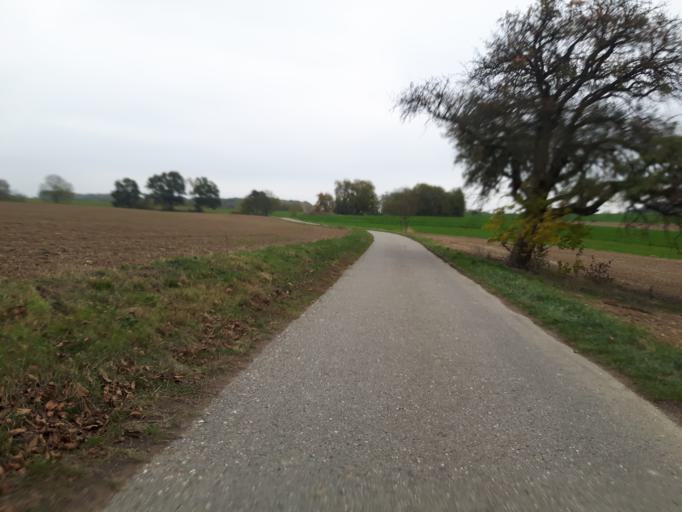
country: DE
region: Baden-Wuerttemberg
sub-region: Karlsruhe Region
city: Ostringen
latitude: 49.2068
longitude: 8.7261
